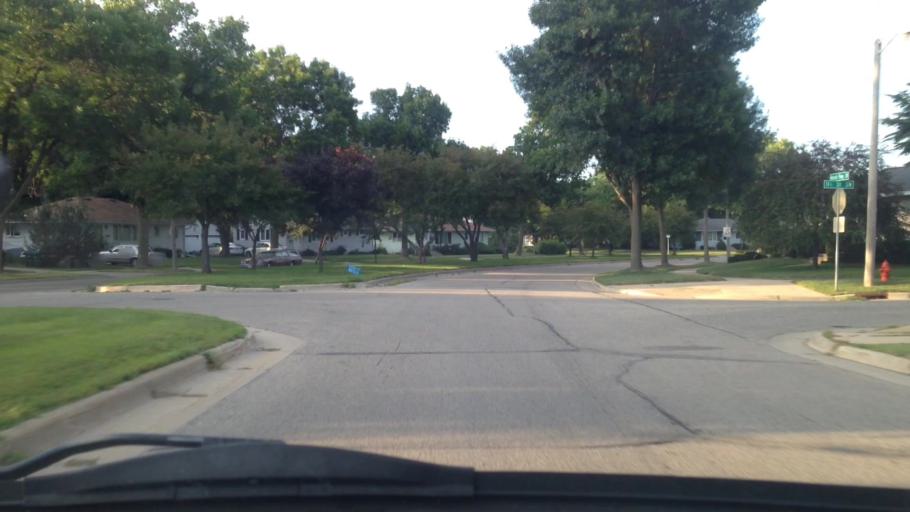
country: US
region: Minnesota
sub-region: Olmsted County
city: Rochester
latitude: 44.0080
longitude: -92.4775
